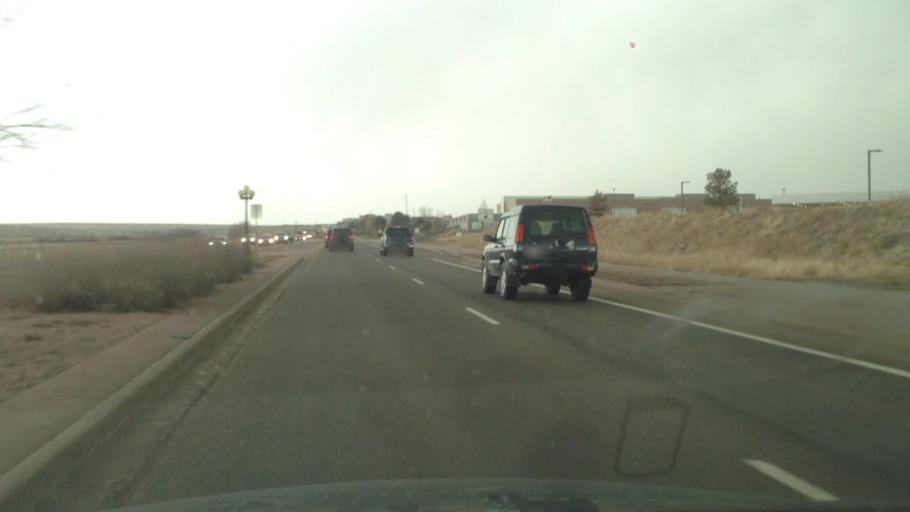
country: US
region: Colorado
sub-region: Douglas County
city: Parker
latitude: 39.4931
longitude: -104.7843
